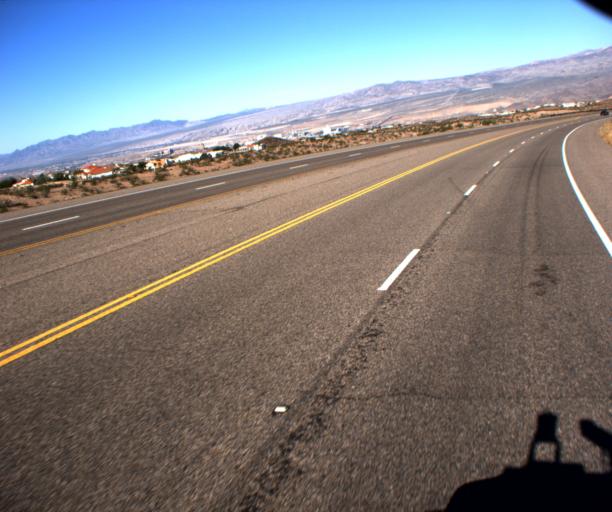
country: US
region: Nevada
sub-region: Clark County
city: Laughlin
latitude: 35.1847
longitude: -114.4965
